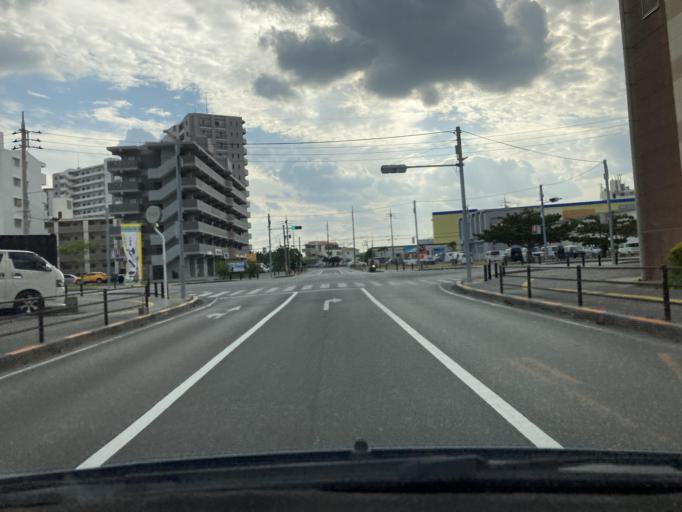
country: JP
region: Okinawa
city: Itoman
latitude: 26.1579
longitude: 127.6599
